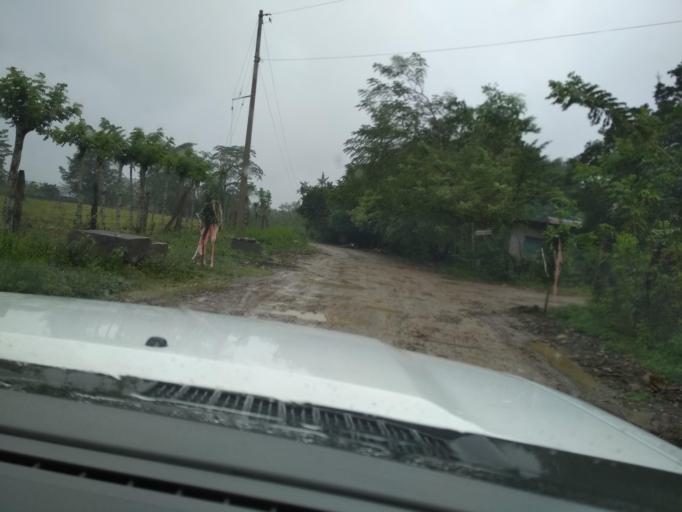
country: MX
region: Veracruz
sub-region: Chalma
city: San Pedro Coyutla
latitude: 21.2487
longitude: -98.4646
